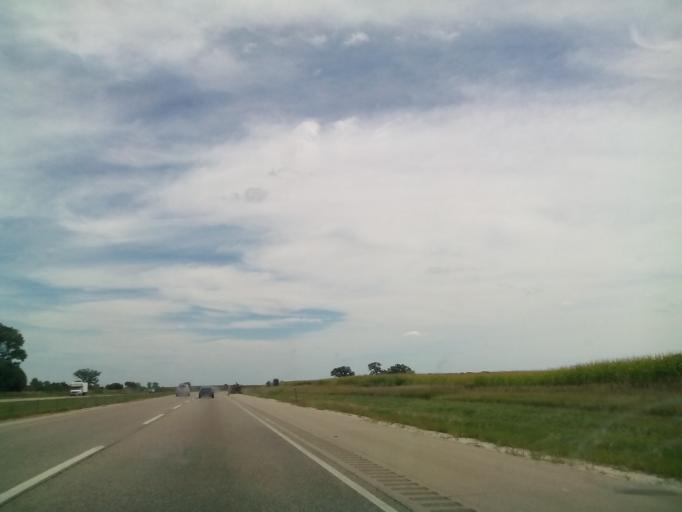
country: US
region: Illinois
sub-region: Kane County
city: Maple Park
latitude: 41.8667
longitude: -88.5726
